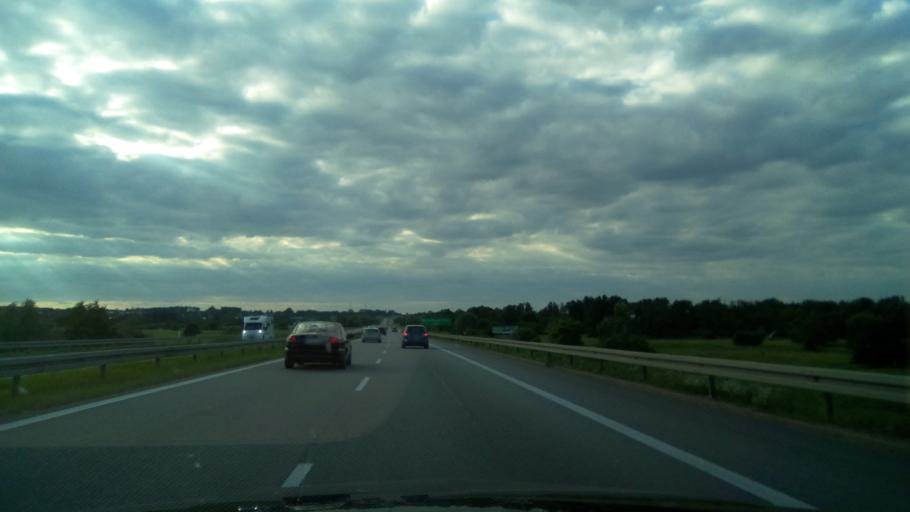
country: PL
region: Masovian Voivodeship
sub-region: Powiat bialobrzeski
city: Bialobrzegi
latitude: 51.6583
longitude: 20.9641
